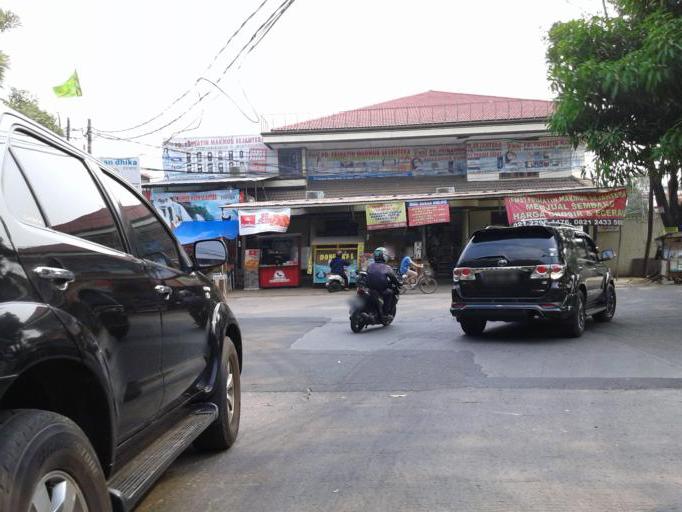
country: ID
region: West Java
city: Pamulang
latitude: -6.3450
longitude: 106.7779
